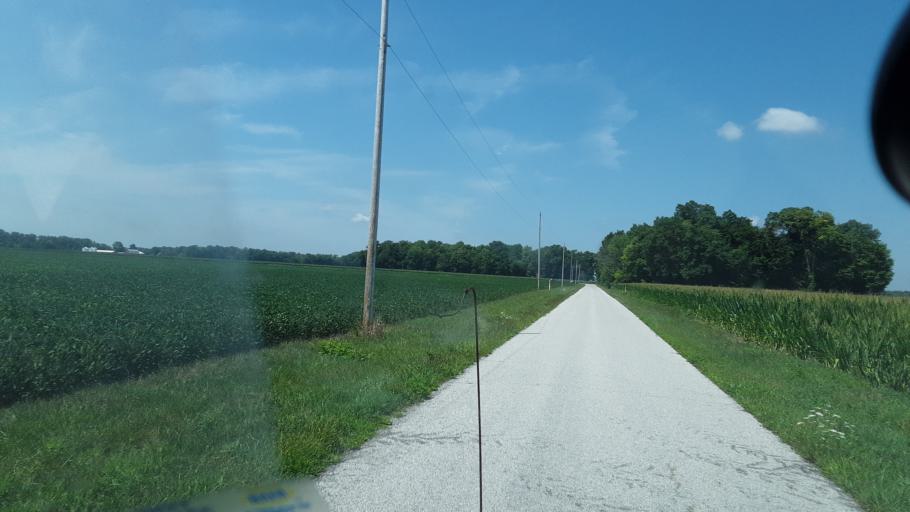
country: US
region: Ohio
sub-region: Hancock County
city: Findlay
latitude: 40.9922
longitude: -83.5306
